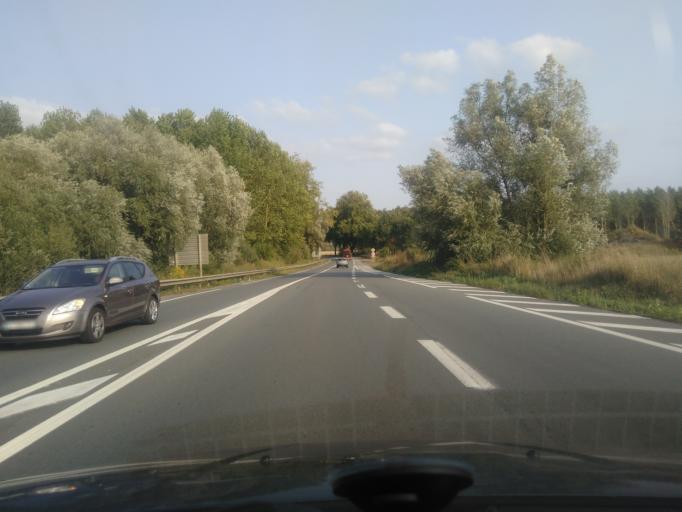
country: FR
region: Picardie
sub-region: Departement de l'Aisne
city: Laon
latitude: 49.5473
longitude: 3.6030
